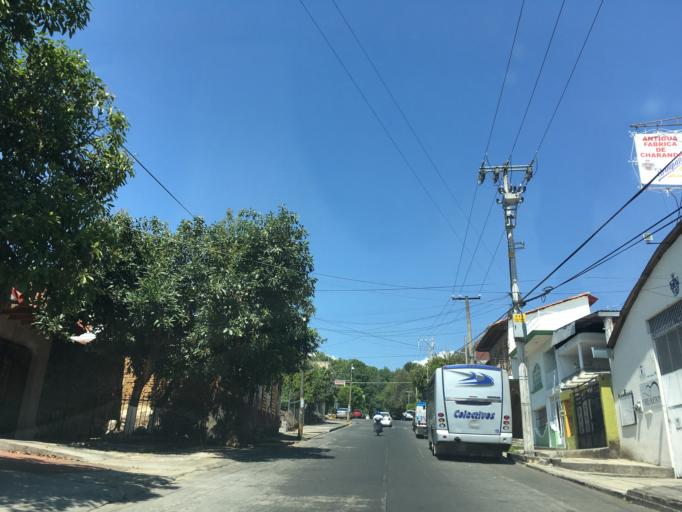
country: MX
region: Michoacan
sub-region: Uruapan
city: Uruapan
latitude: 19.4247
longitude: -102.0689
